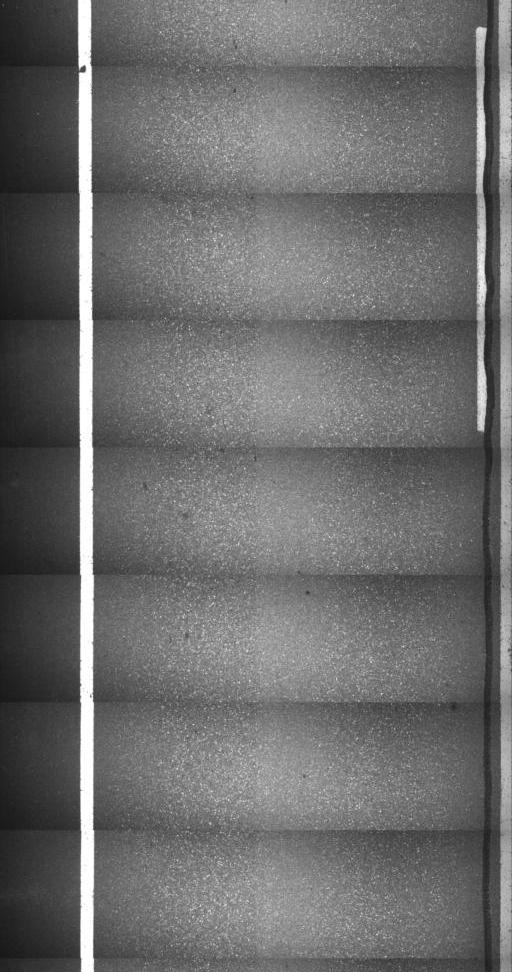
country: US
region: Vermont
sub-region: Lamoille County
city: Morrisville
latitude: 44.5338
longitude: -72.5193
